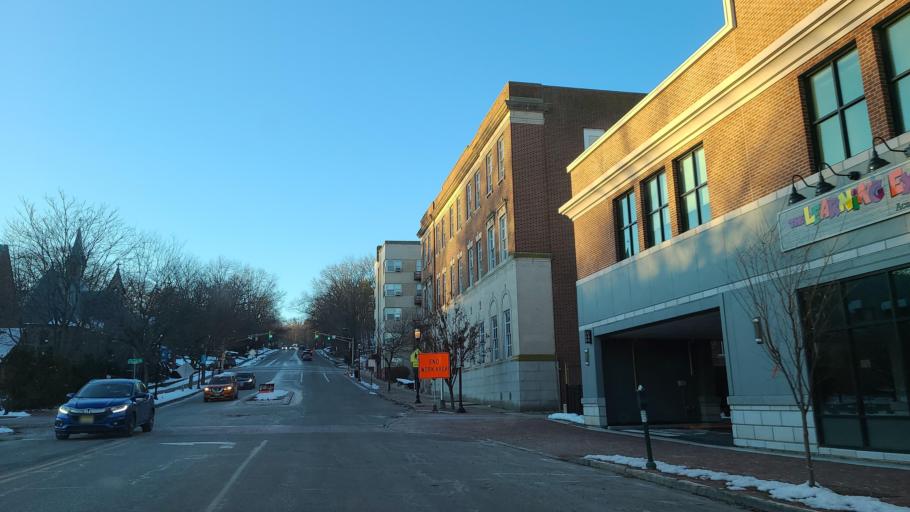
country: US
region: New Jersey
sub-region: Essex County
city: South Orange
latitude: 40.7471
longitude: -74.2621
